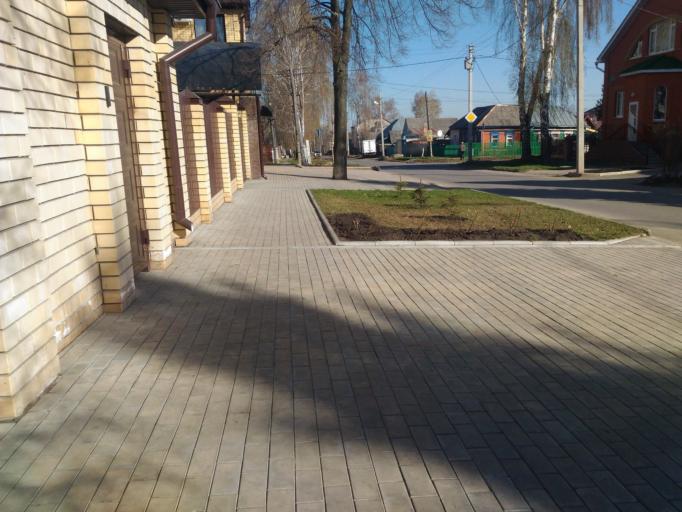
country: RU
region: Ulyanovsk
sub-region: Ulyanovskiy Rayon
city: Ulyanovsk
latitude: 54.3486
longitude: 48.3787
